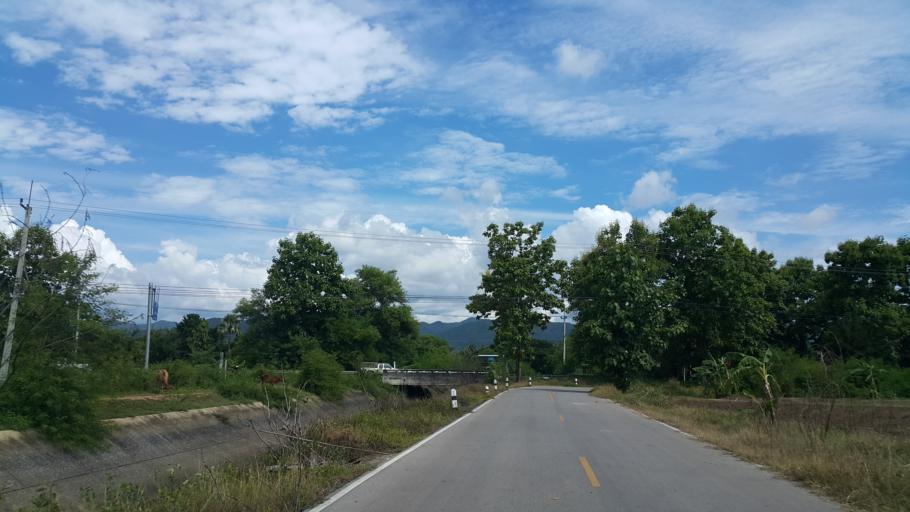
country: TH
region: Chiang Mai
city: Mae On
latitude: 18.7413
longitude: 99.2015
